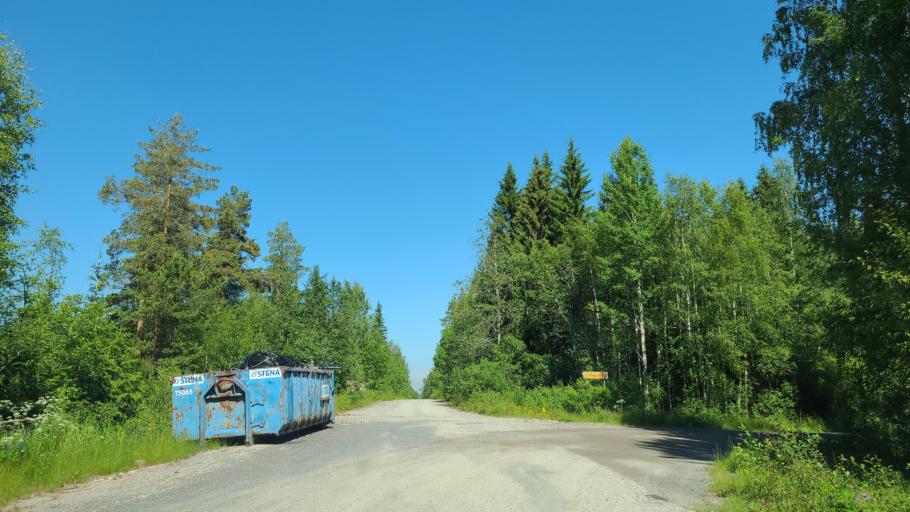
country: SE
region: Vaesternorrland
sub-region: OErnskoeldsviks Kommun
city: Husum
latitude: 63.4171
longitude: 19.2213
